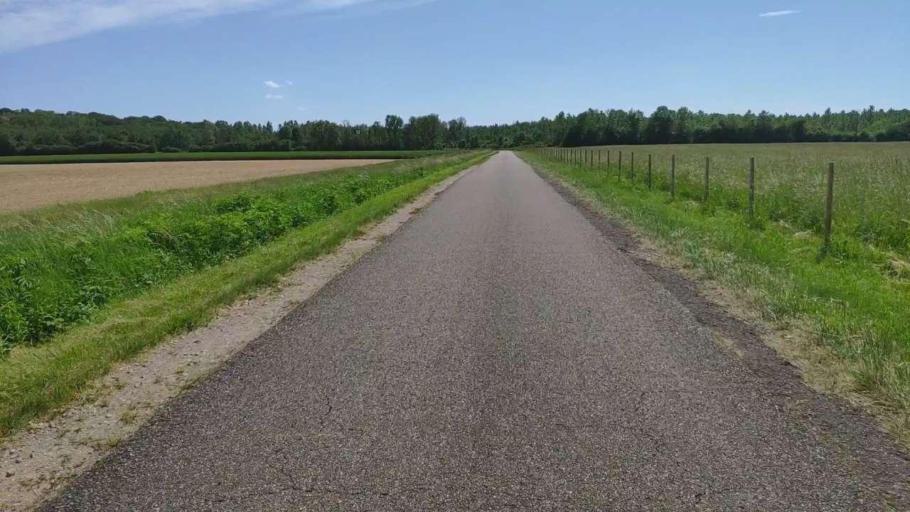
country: FR
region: Franche-Comte
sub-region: Departement du Jura
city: Bletterans
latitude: 46.7269
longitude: 5.4786
